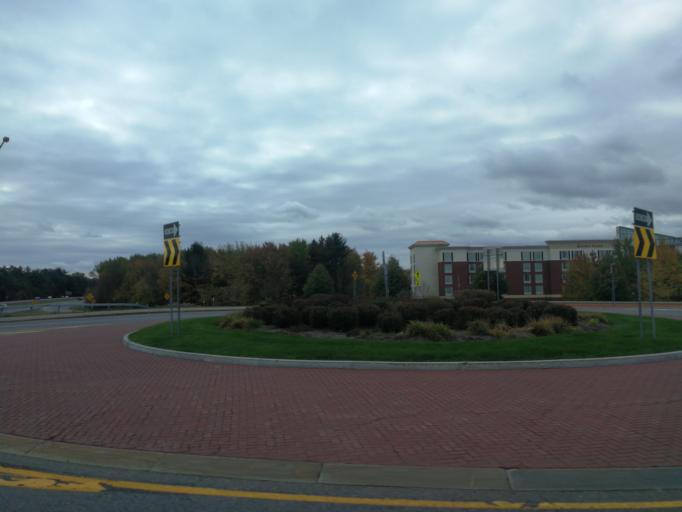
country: US
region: New York
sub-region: Saratoga County
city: Ballston Spa
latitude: 42.9704
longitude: -73.8030
